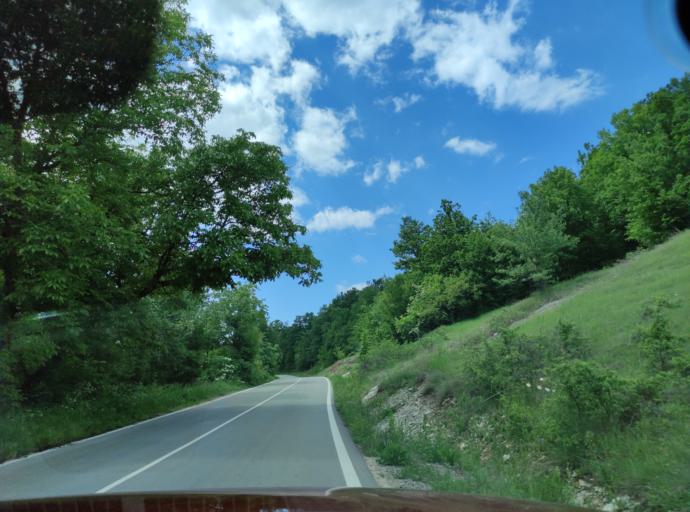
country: BG
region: Montana
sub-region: Obshtina Chiprovtsi
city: Chiprovtsi
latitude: 43.4543
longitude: 22.9042
